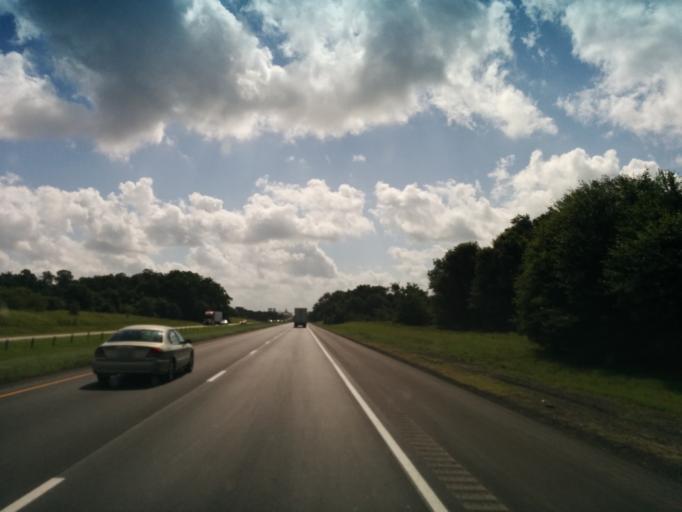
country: US
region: Texas
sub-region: Colorado County
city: Weimar
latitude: 29.6897
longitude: -96.8041
